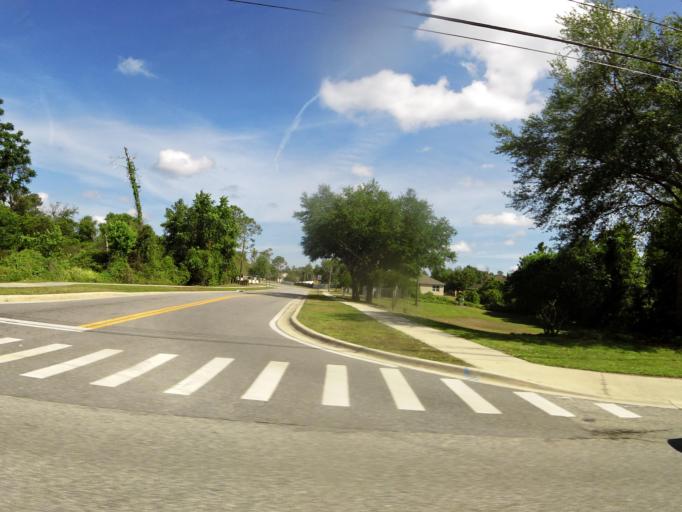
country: US
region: Florida
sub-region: Volusia County
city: Lake Helen
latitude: 28.9478
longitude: -81.2372
